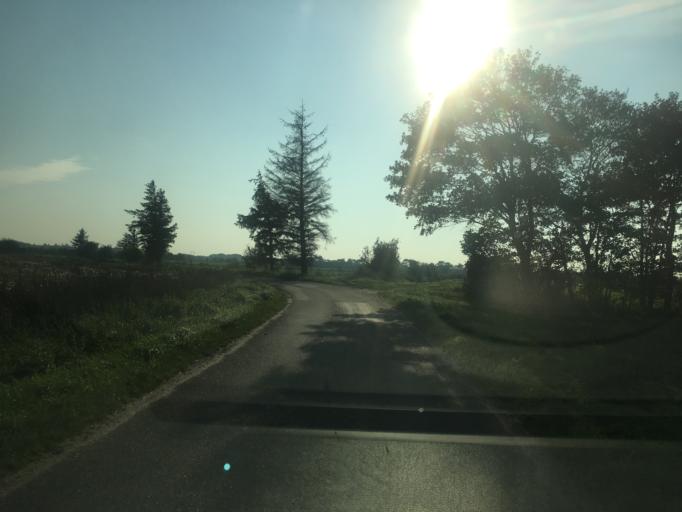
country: DE
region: Schleswig-Holstein
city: Bramstedtlund
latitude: 54.9686
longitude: 9.0709
